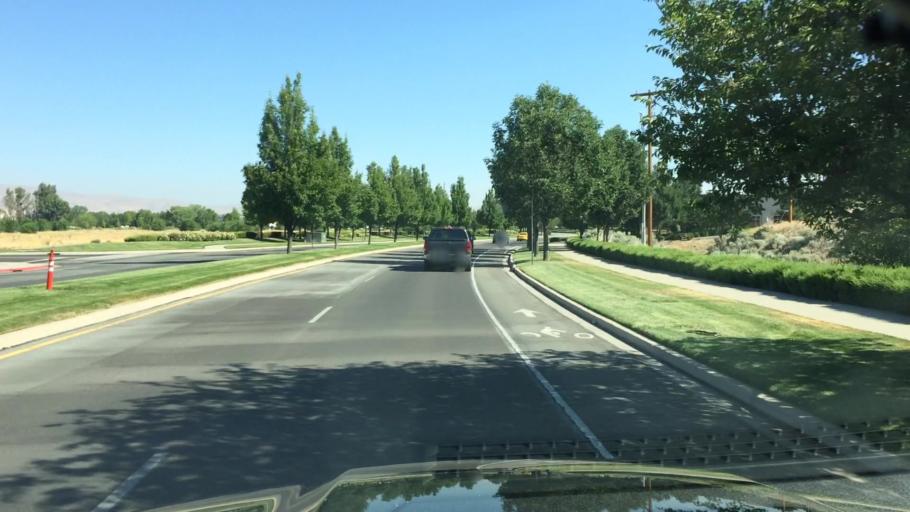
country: US
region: Nevada
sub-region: Washoe County
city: Sparks
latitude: 39.4639
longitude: -119.7661
